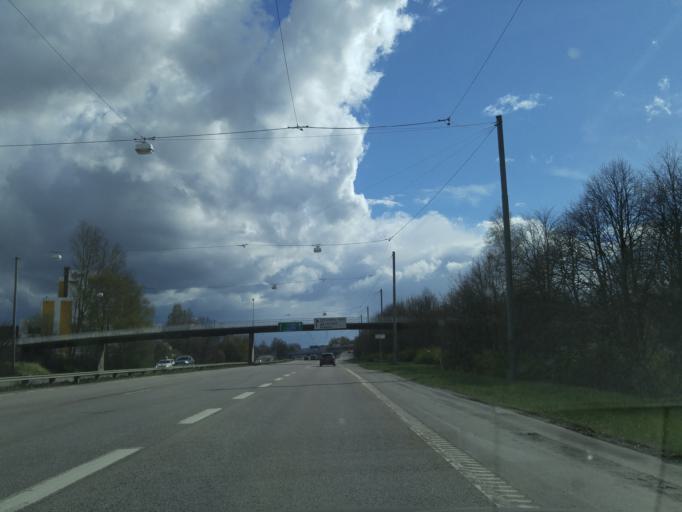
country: SE
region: Vaestra Goetaland
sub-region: Goteborg
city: Majorna
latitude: 57.6649
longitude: 11.9366
